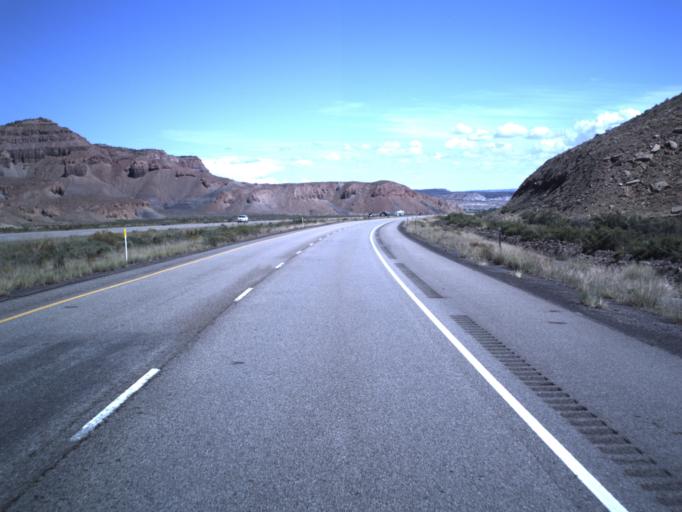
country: US
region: Utah
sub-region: Emery County
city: Ferron
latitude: 38.8090
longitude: -111.2543
